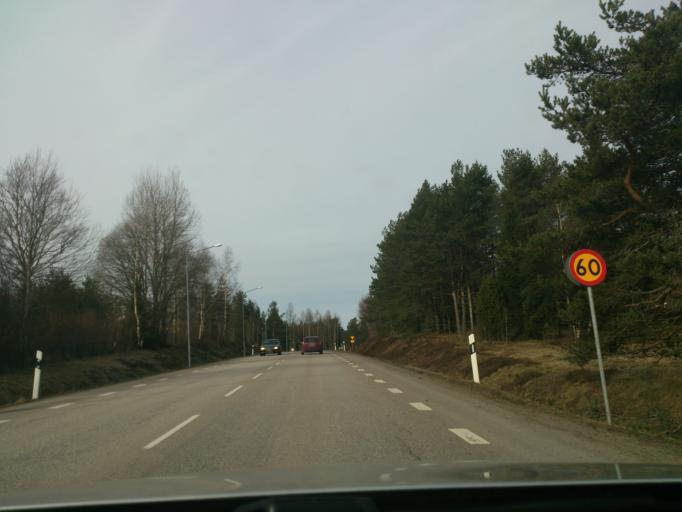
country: SE
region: Kronoberg
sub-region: Alvesta Kommun
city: Moheda
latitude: 56.9998
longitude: 14.5637
